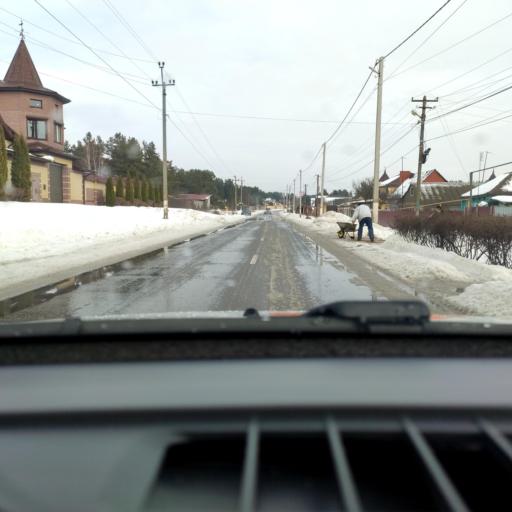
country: RU
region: Voronezj
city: Podgornoye
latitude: 51.7751
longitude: 39.1267
